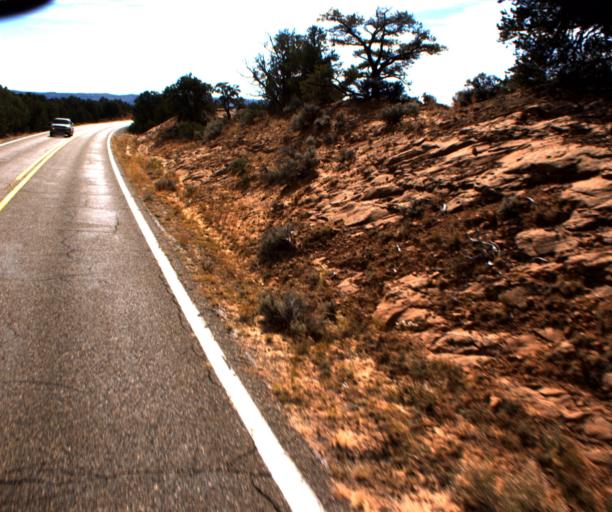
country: US
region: Arizona
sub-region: Navajo County
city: Kayenta
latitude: 36.6411
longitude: -110.5125
